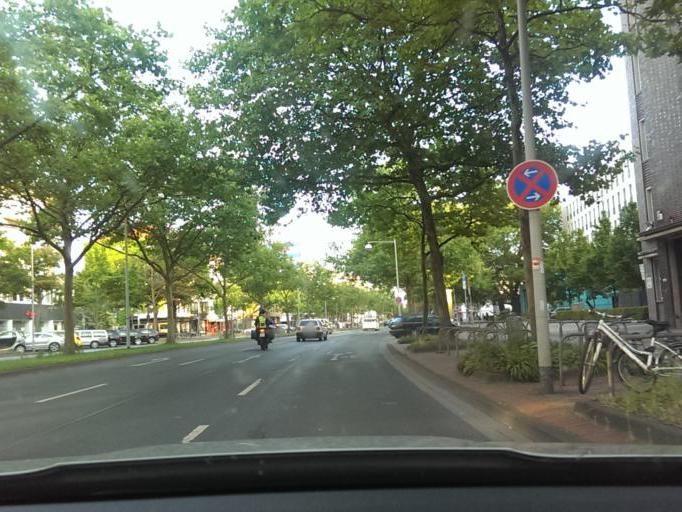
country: DE
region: Lower Saxony
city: Hannover
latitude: 52.3672
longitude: 9.7451
